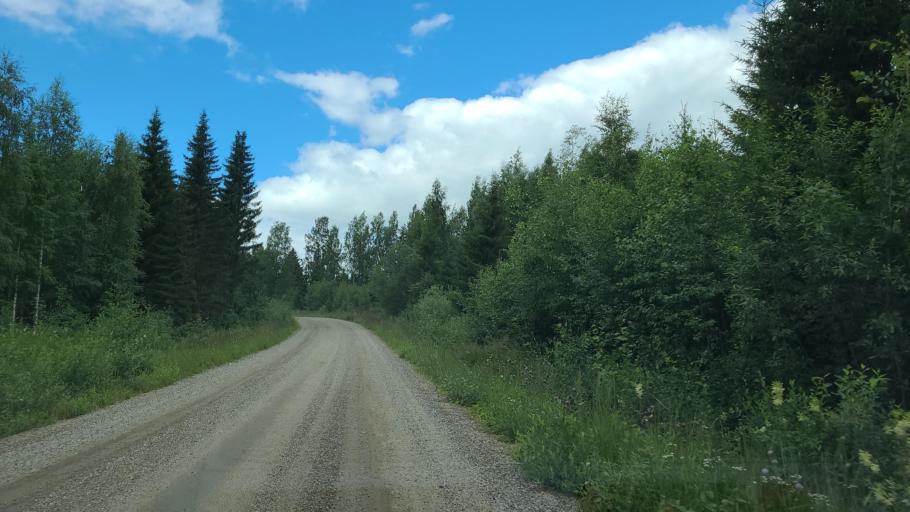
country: FI
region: Northern Savo
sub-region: Koillis-Savo
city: Kaavi
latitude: 62.9934
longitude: 28.5414
